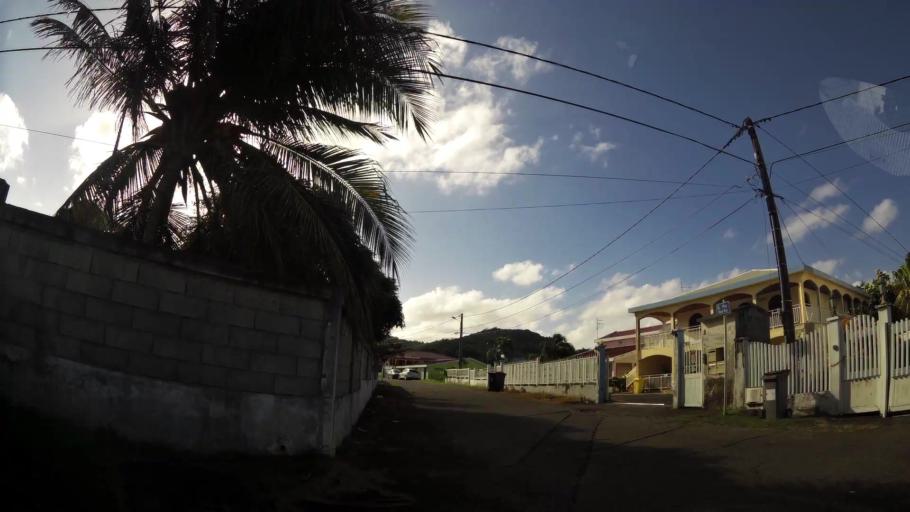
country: MQ
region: Martinique
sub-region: Martinique
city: Le Francois
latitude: 14.6197
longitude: -60.8964
